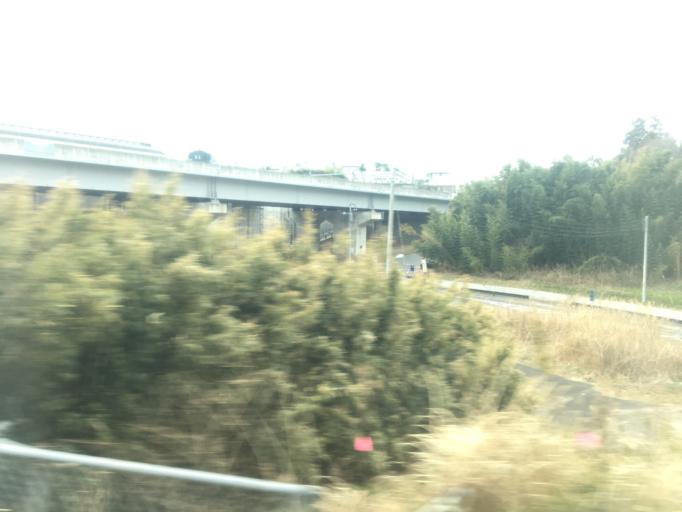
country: JP
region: Chiba
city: Narita
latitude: 35.8004
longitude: 140.2914
